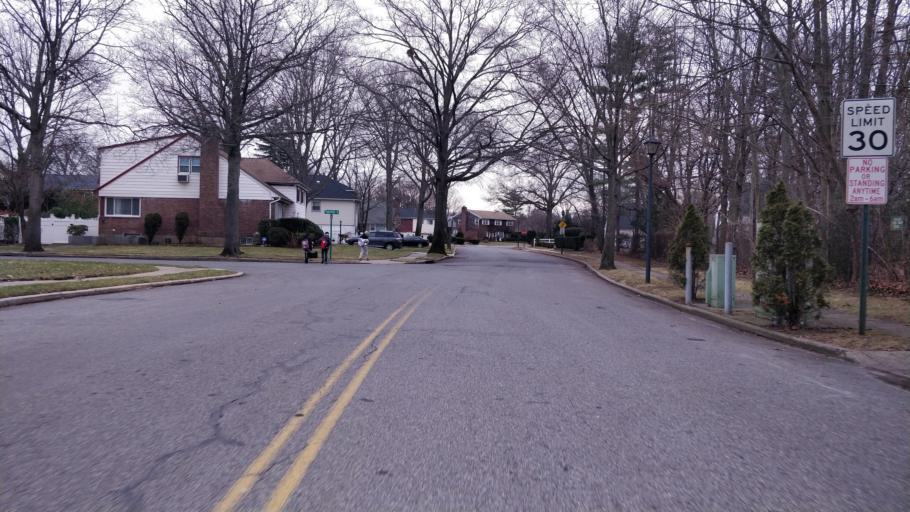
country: US
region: New York
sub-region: Nassau County
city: New Cassel
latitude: 40.7678
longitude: -73.5765
